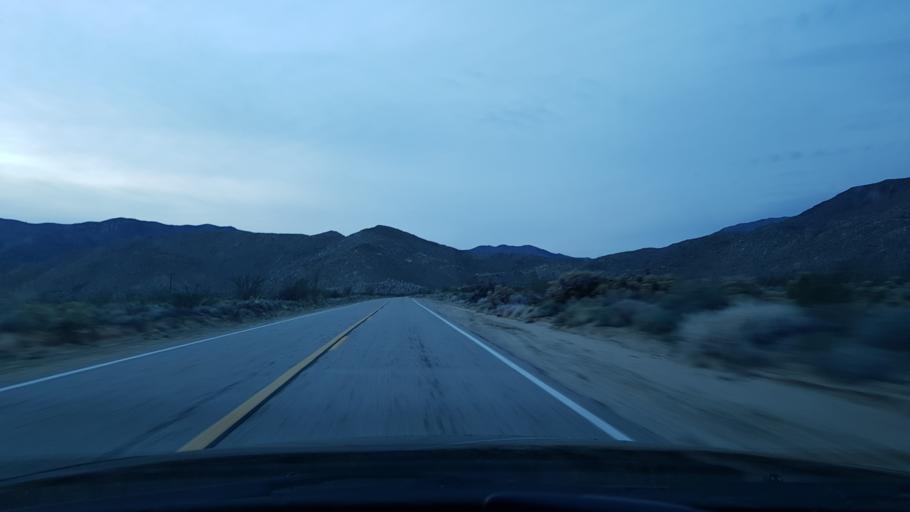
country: US
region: California
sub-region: San Diego County
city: Pine Valley
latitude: 32.9717
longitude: -116.4016
